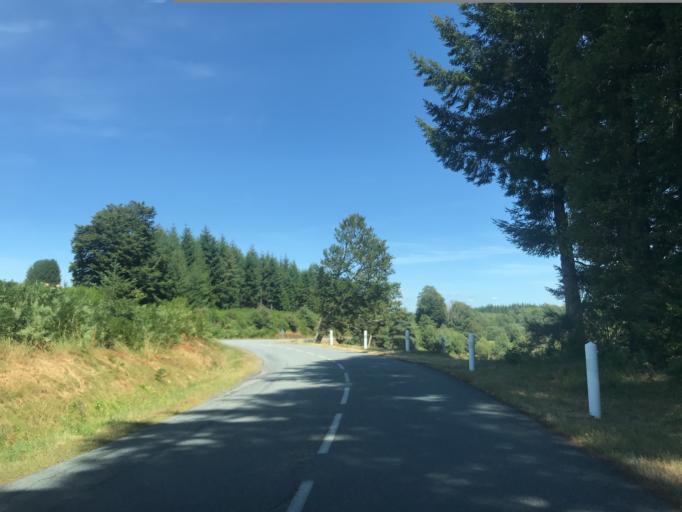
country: FR
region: Limousin
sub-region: Departement de la Creuse
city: Felletin
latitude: 45.7764
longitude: 2.1357
